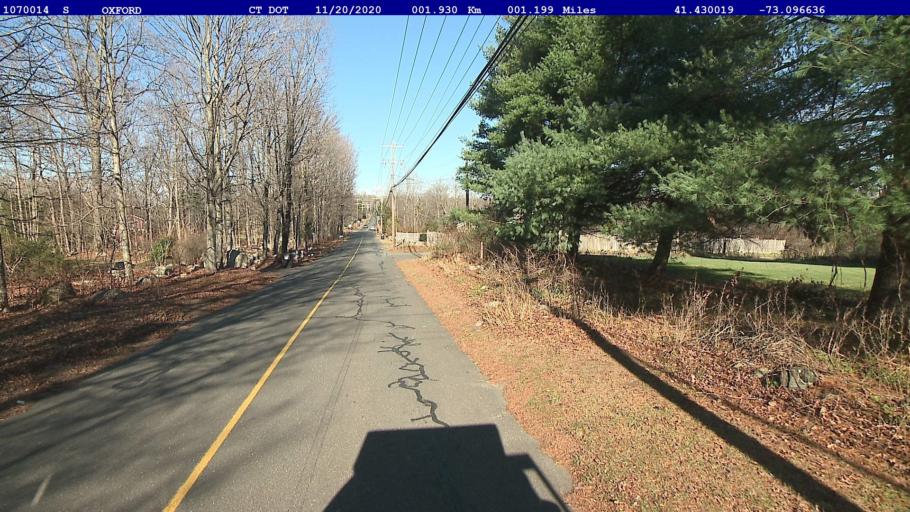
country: US
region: Connecticut
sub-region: New Haven County
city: Oxford
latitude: 41.4300
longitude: -73.0966
